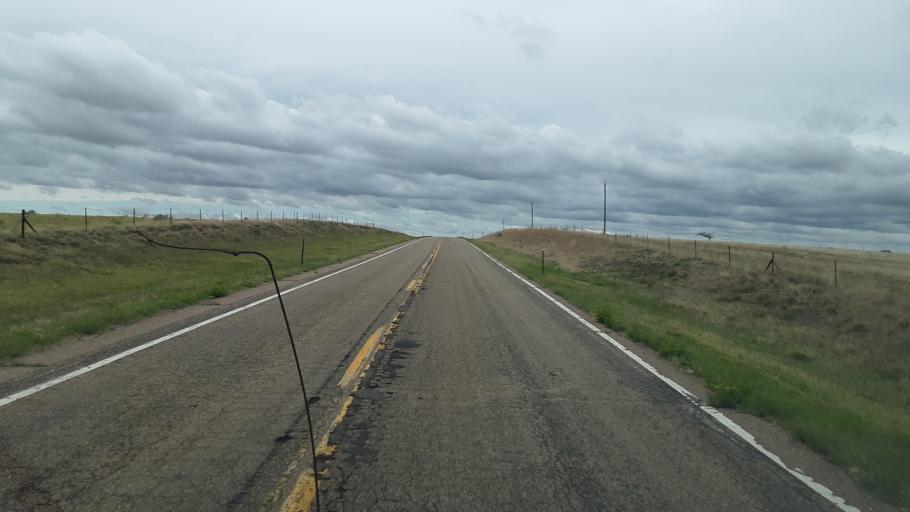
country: US
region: Colorado
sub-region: Lincoln County
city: Limon
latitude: 38.8385
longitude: -103.8724
